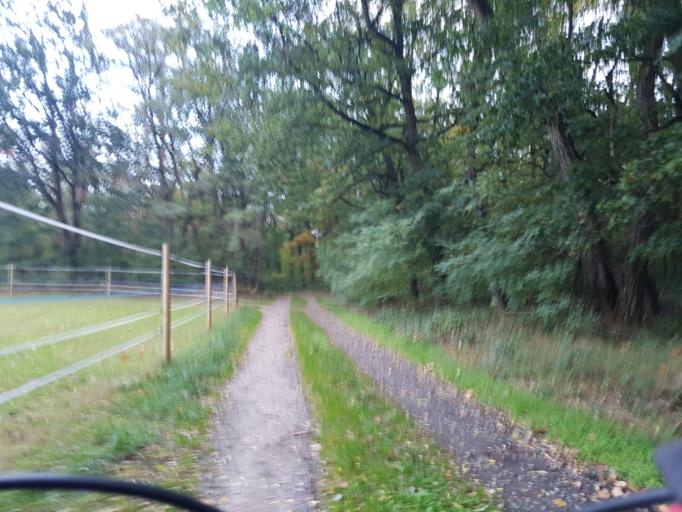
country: DE
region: Brandenburg
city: Bad Liebenwerda
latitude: 51.5411
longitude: 13.4194
